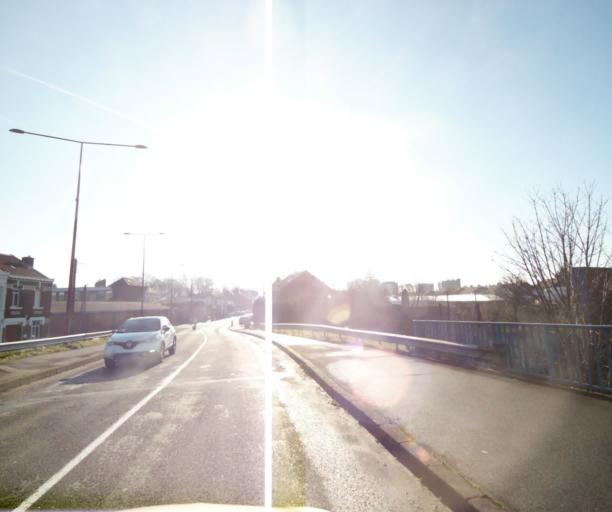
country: FR
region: Nord-Pas-de-Calais
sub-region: Departement du Nord
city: Aulnoy-lez-Valenciennes
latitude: 50.3379
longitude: 3.5243
